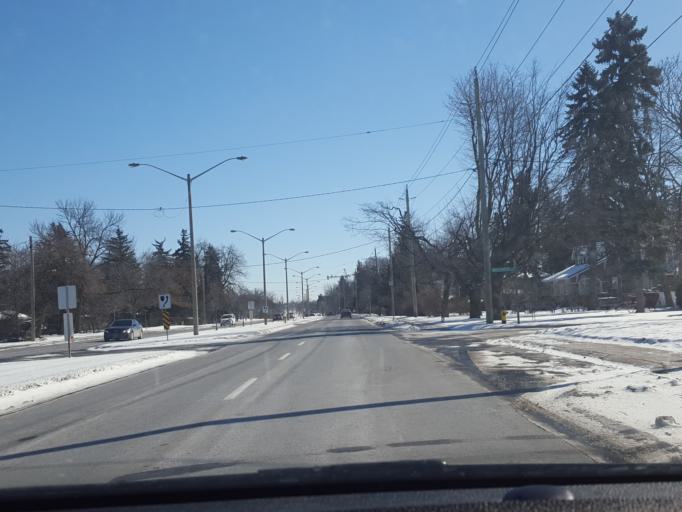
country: CA
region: Ontario
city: Cambridge
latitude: 43.3849
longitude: -80.3379
